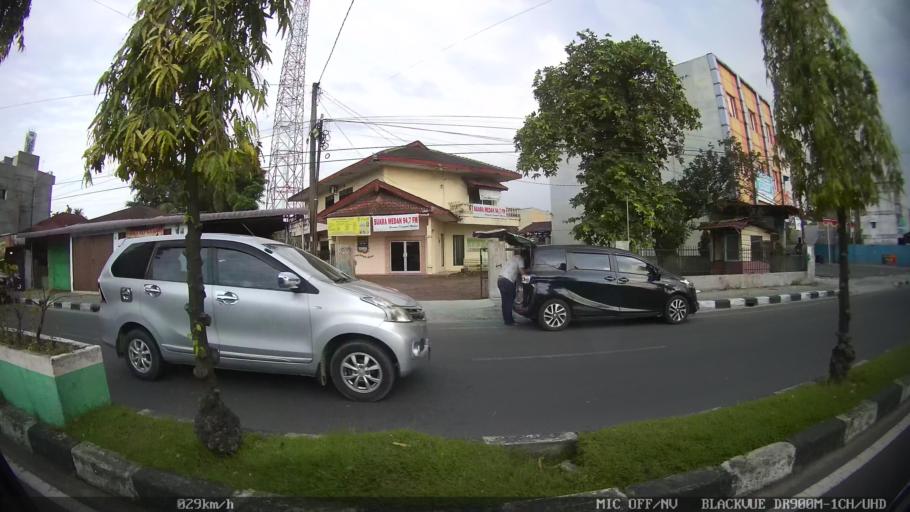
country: ID
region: North Sumatra
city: Sunggal
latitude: 3.5592
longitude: 98.6358
